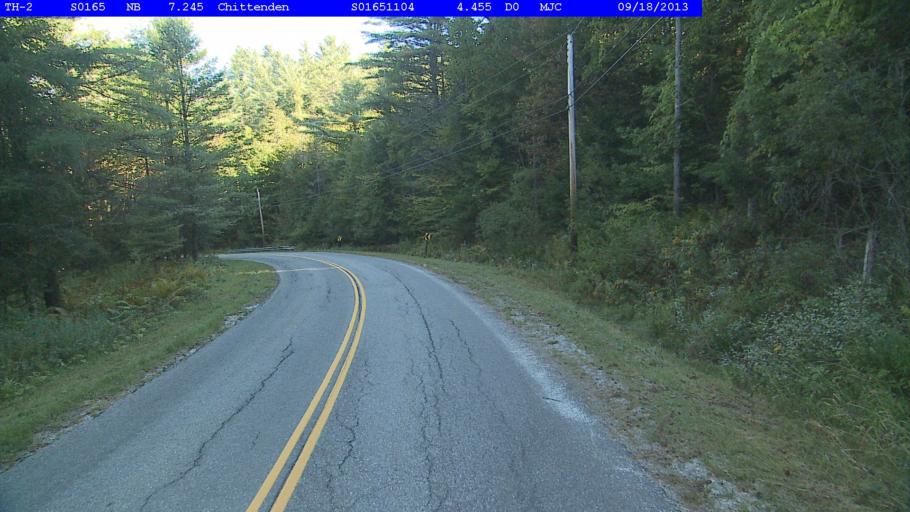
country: US
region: Vermont
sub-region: Rutland County
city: Rutland
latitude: 43.7380
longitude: -72.9705
